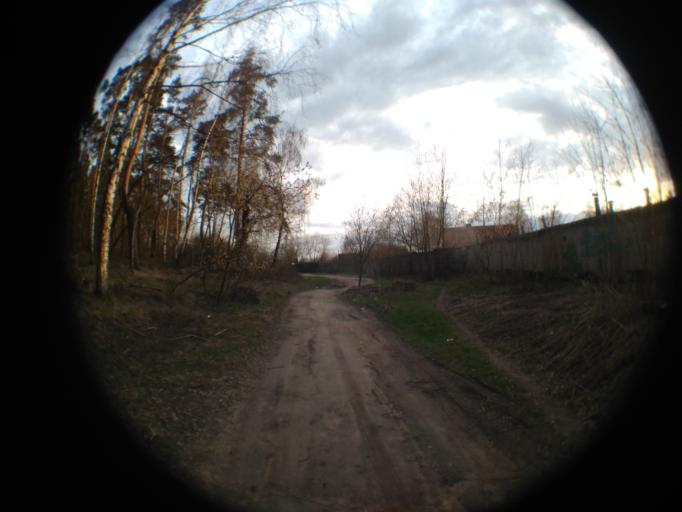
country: RU
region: Moskovskaya
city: Zhukovskiy
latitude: 55.5853
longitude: 38.1092
